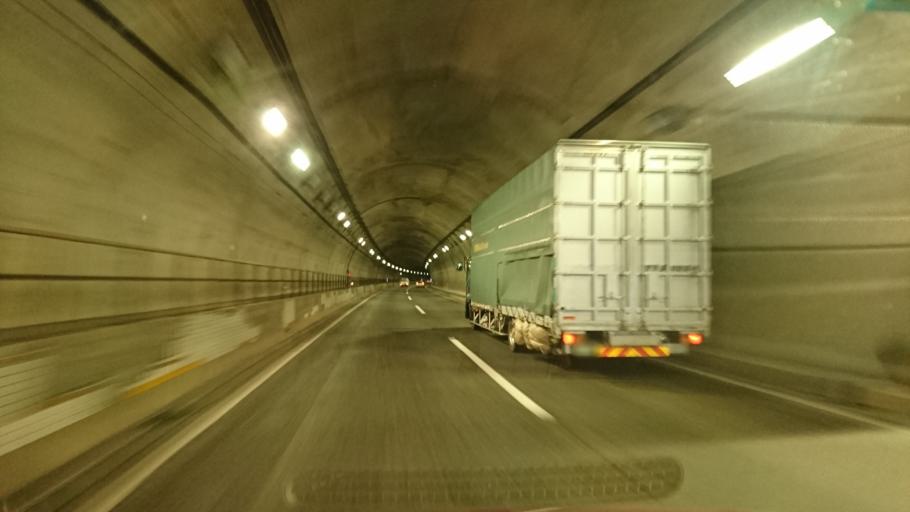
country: JP
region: Okayama
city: Okayama-shi
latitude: 34.7236
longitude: 133.9631
